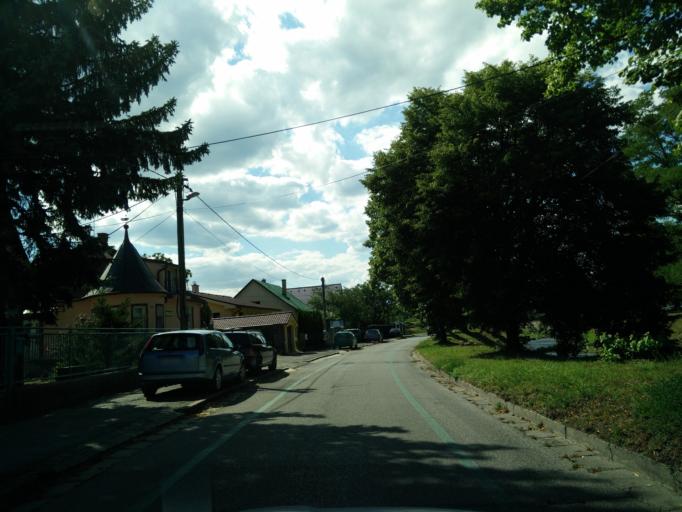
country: SK
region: Nitriansky
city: Prievidza
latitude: 48.7690
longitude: 18.6173
